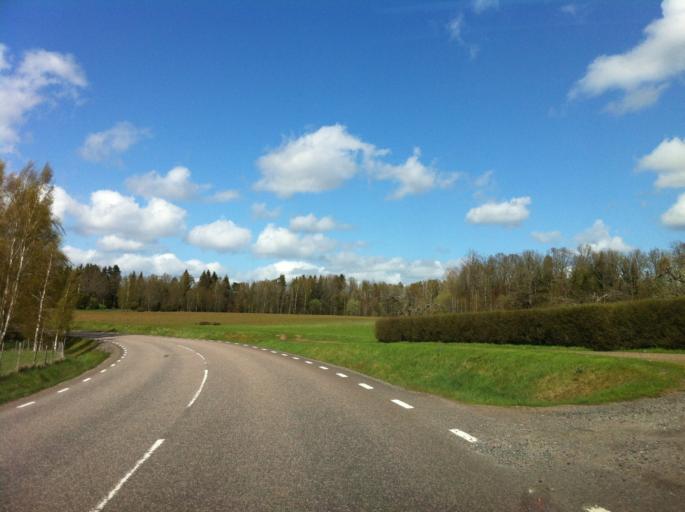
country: SE
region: Vaestra Goetaland
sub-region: Alingsas Kommun
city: Alingsas
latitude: 57.8654
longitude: 12.5711
